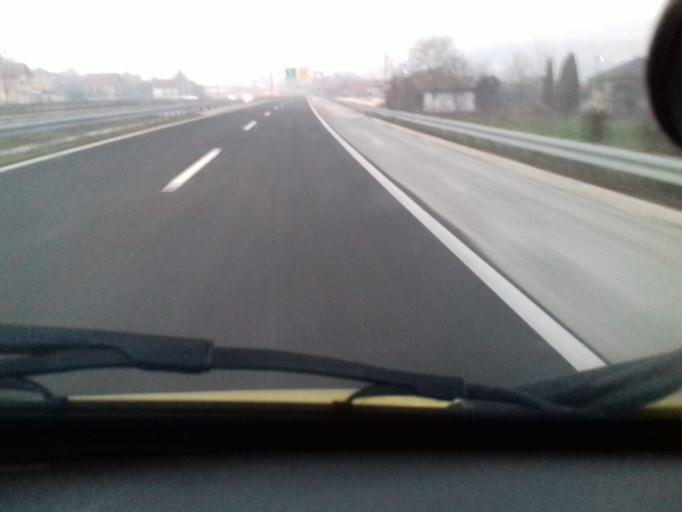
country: BA
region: Federation of Bosnia and Herzegovina
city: Kakanj
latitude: 44.1204
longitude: 18.1035
